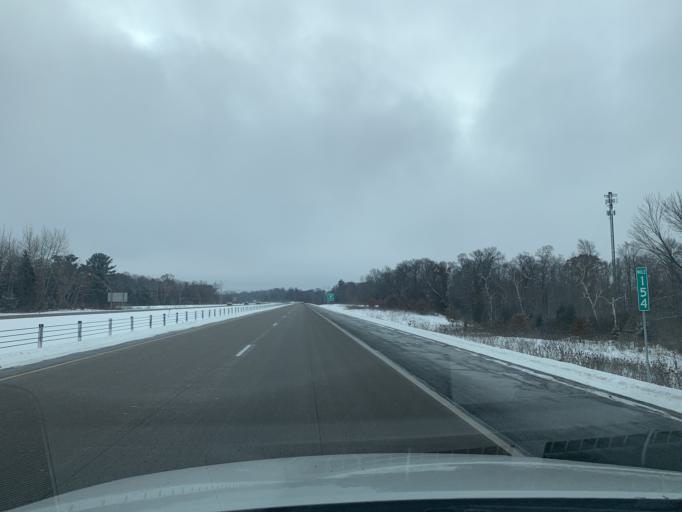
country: US
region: Minnesota
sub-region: Chisago County
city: Harris
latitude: 45.5985
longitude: -92.9955
